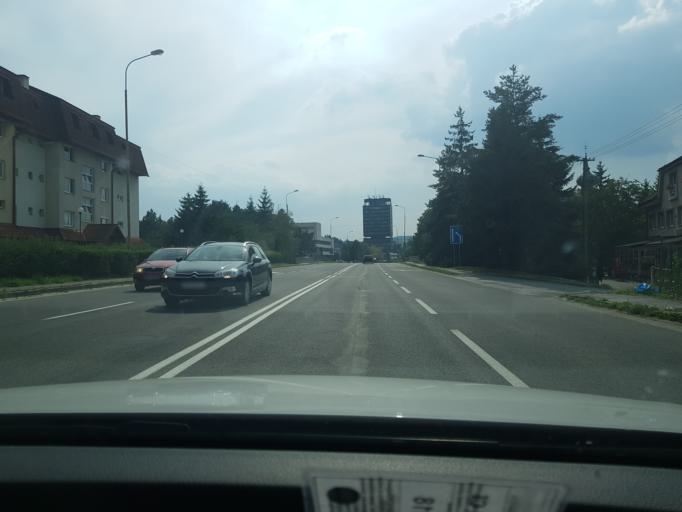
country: SK
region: Trenciansky
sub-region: Okres Povazska Bystrica
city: Povazska Bystrica
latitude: 49.1189
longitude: 18.4529
